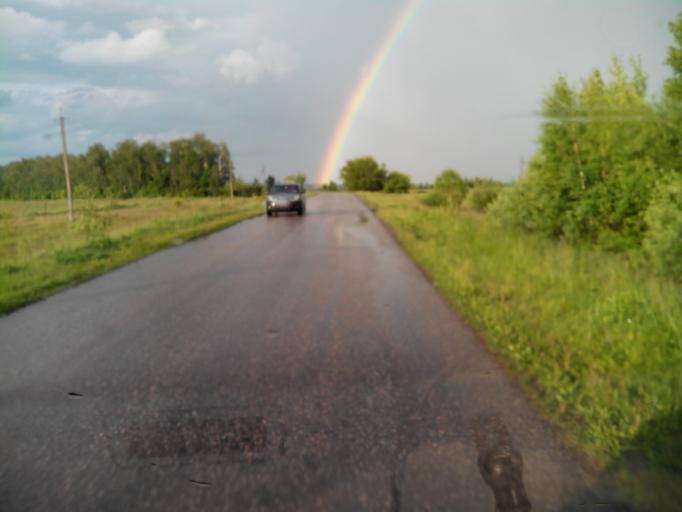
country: RU
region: Penza
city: Zasechnoye
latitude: 53.0595
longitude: 44.9836
